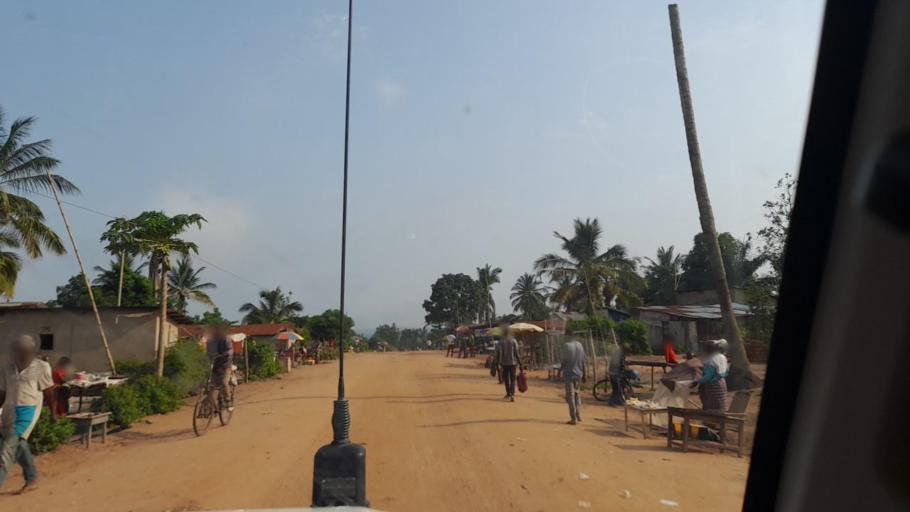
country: CD
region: Kasai-Occidental
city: Kananga
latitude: -5.8965
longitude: 22.3755
